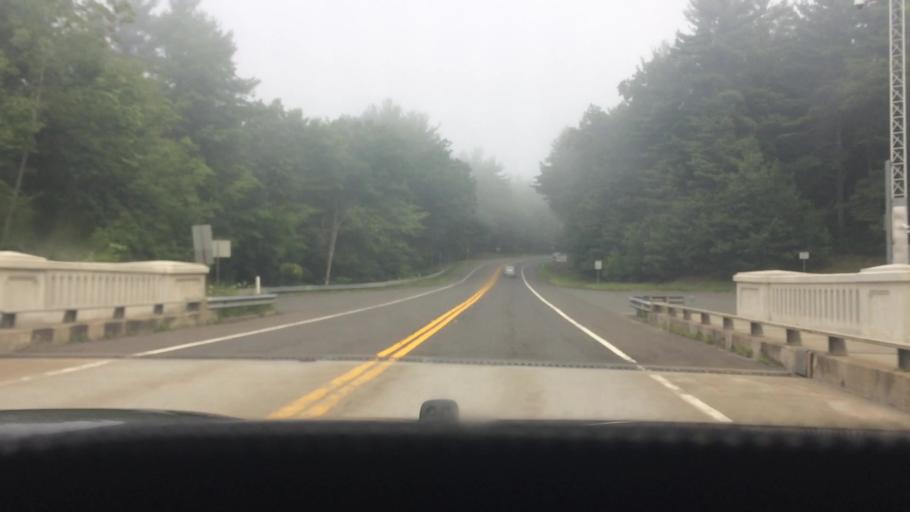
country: US
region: Massachusetts
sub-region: Franklin County
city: Millers Falls
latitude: 42.5983
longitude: -72.4980
